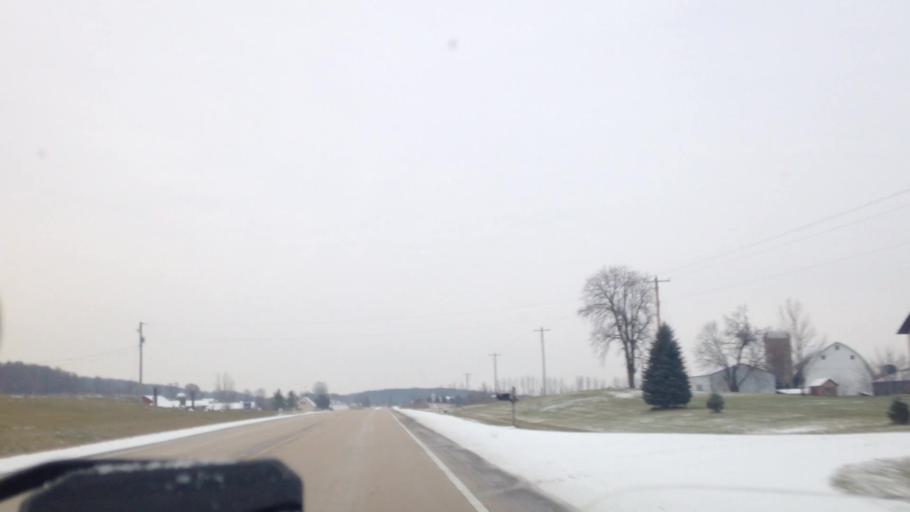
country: US
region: Wisconsin
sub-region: Dodge County
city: Mayville
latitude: 43.4766
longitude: -88.5460
